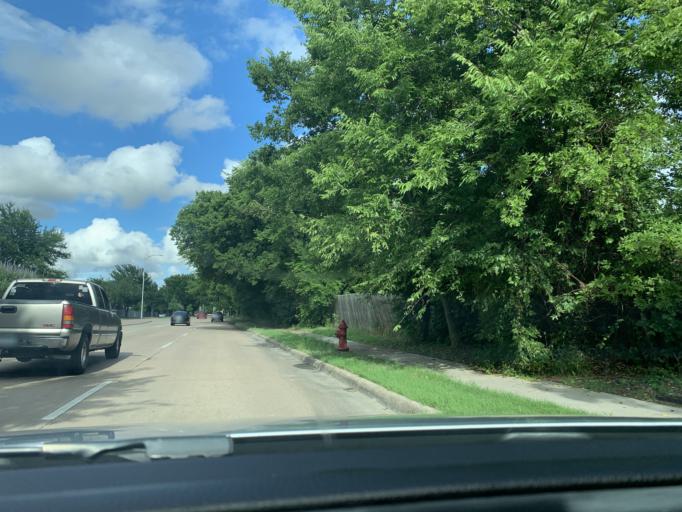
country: US
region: Texas
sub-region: Dallas County
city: Grand Prairie
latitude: 32.6583
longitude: -97.0140
